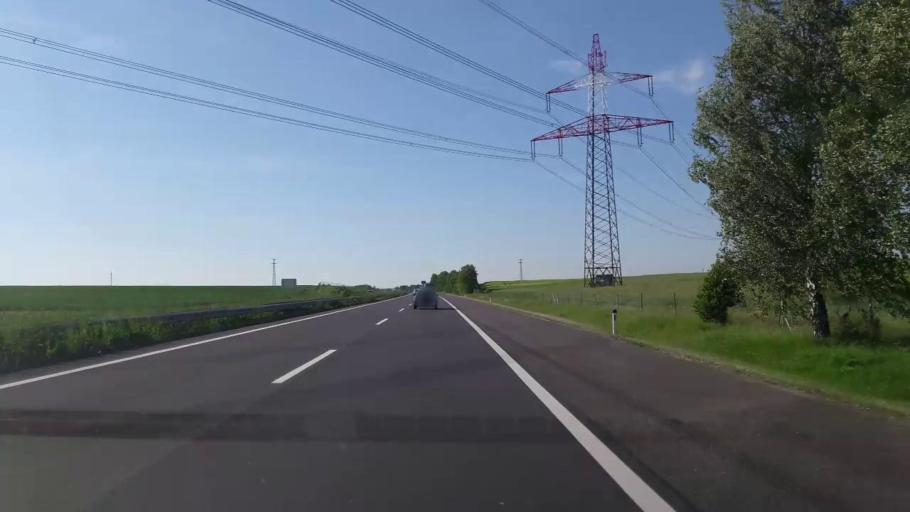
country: AT
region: Burgenland
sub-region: Eisenstadt-Umgebung
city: Hornstein
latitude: 47.8757
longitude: 16.4162
